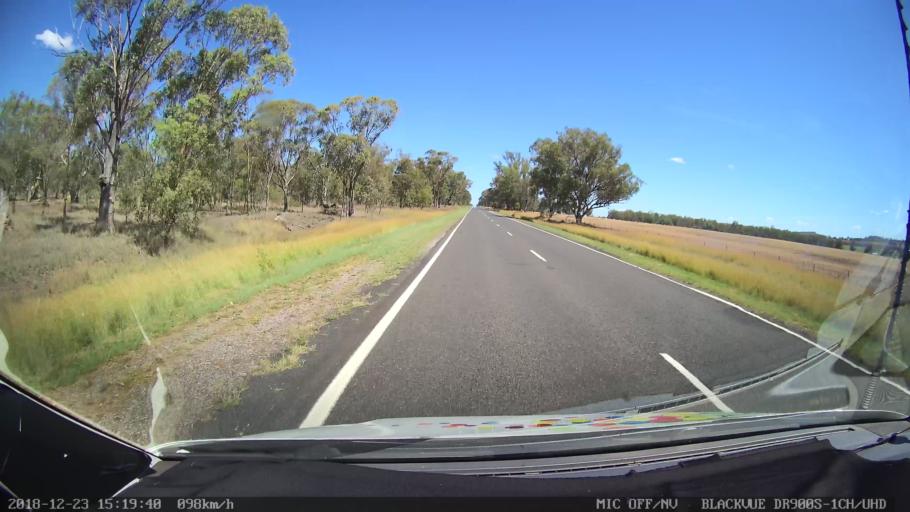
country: AU
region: New South Wales
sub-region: Tamworth Municipality
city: Manilla
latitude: -30.8322
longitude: 150.7844
